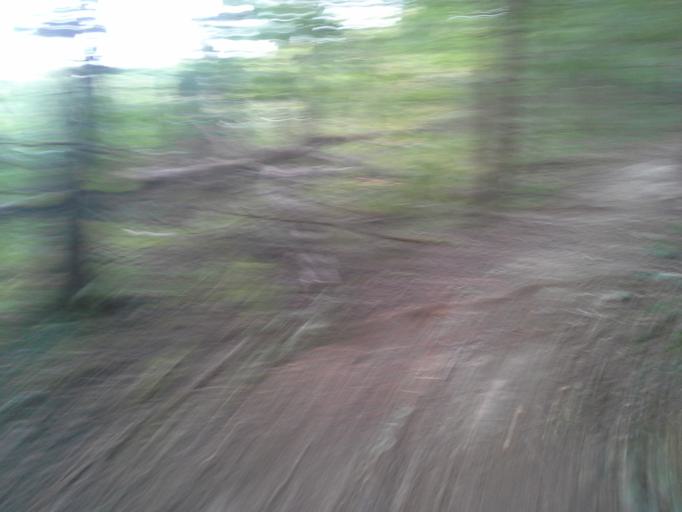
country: RU
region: Moskovskaya
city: Selyatino
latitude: 55.5518
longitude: 37.0017
